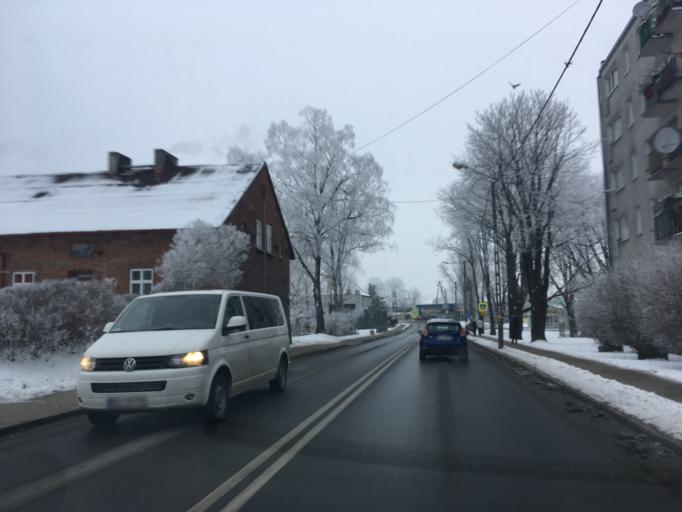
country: PL
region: Warmian-Masurian Voivodeship
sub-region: Powiat olsztynski
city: Biskupiec
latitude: 53.8654
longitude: 20.9612
